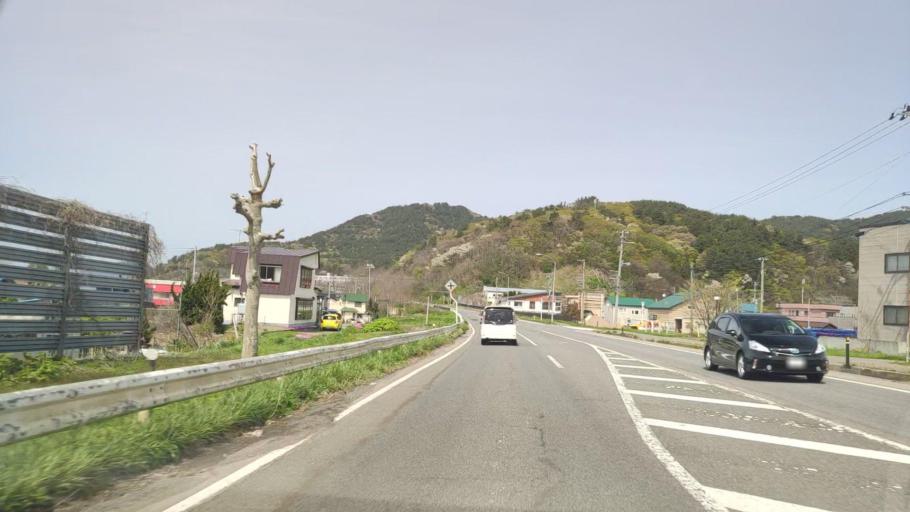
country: JP
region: Aomori
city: Aomori Shi
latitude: 40.8707
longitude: 140.8502
